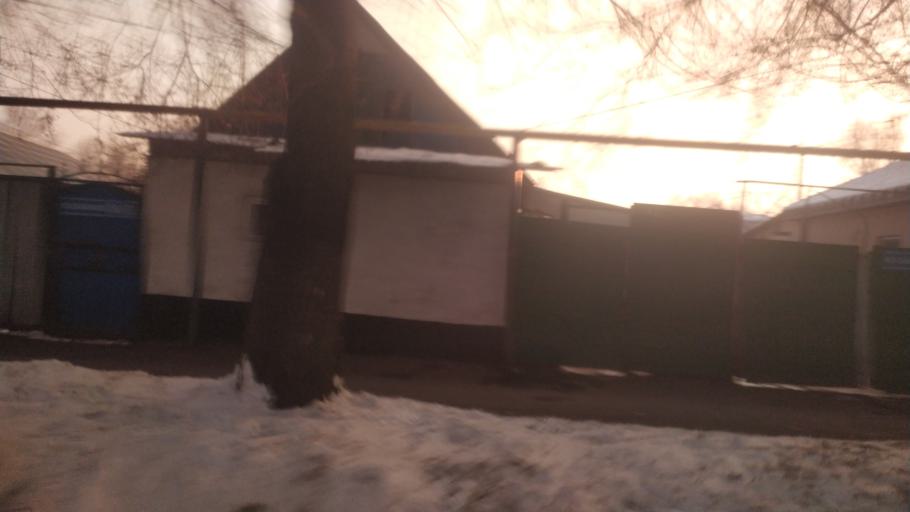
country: KZ
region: Almaty Qalasy
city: Almaty
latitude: 43.2623
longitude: 76.9109
